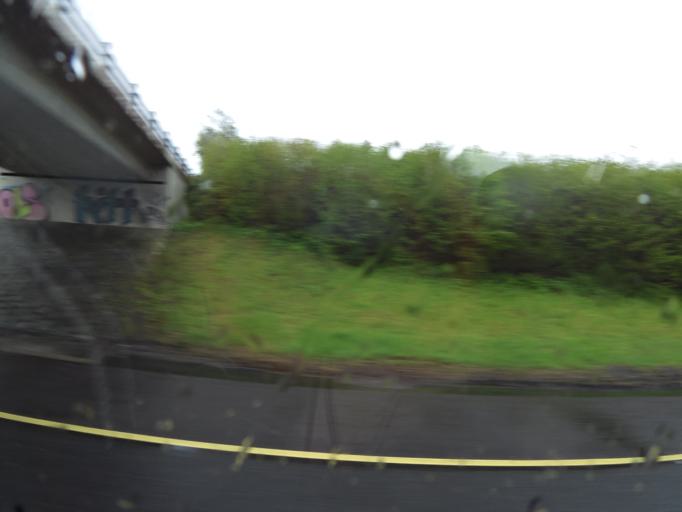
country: IE
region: Leinster
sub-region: Kildare
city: Maynooth
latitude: 53.3650
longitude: -6.5660
